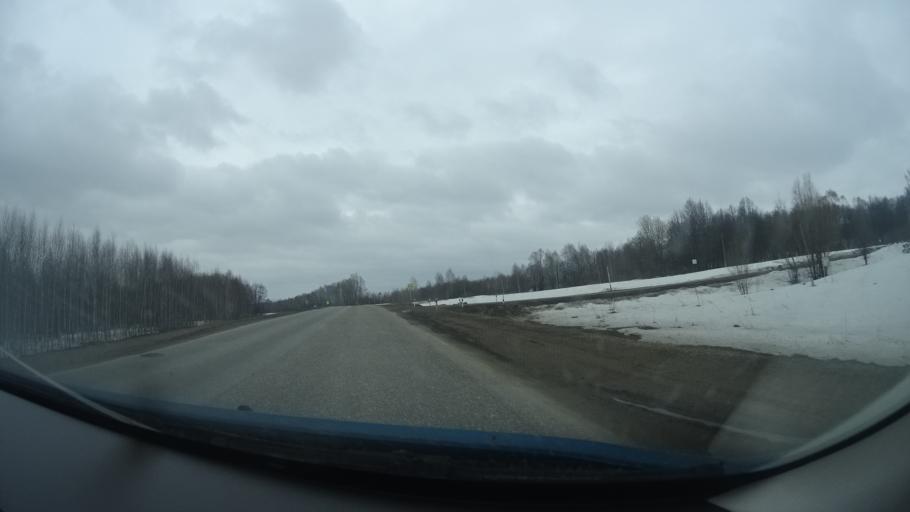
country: RU
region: Bashkortostan
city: Birsk
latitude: 55.2827
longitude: 55.6580
